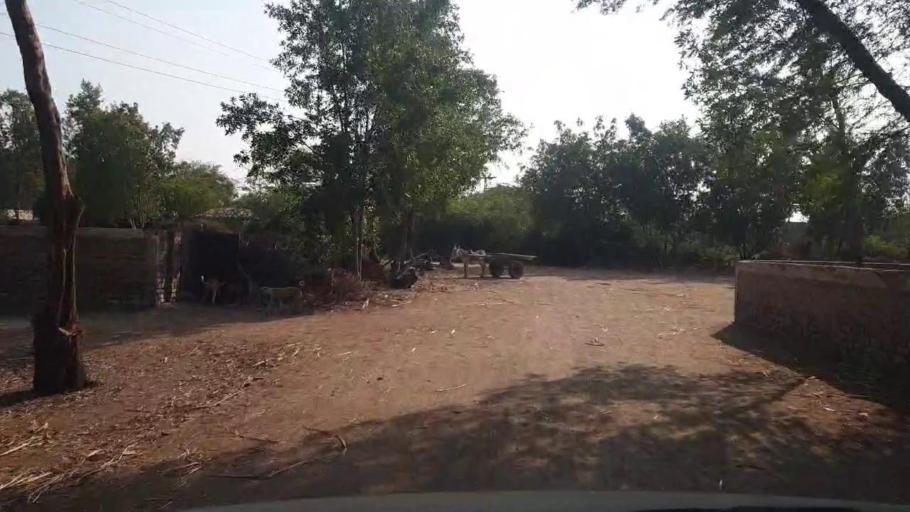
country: PK
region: Sindh
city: Mirwah Gorchani
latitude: 25.2584
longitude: 69.1441
